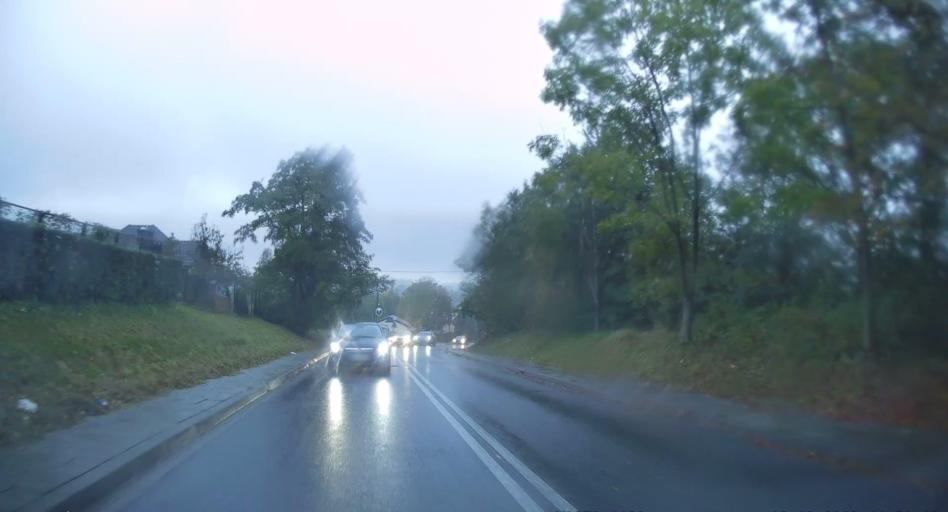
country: PL
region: Lesser Poland Voivodeship
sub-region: Powiat krakowski
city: Ochojno
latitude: 49.9757
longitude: 19.9864
